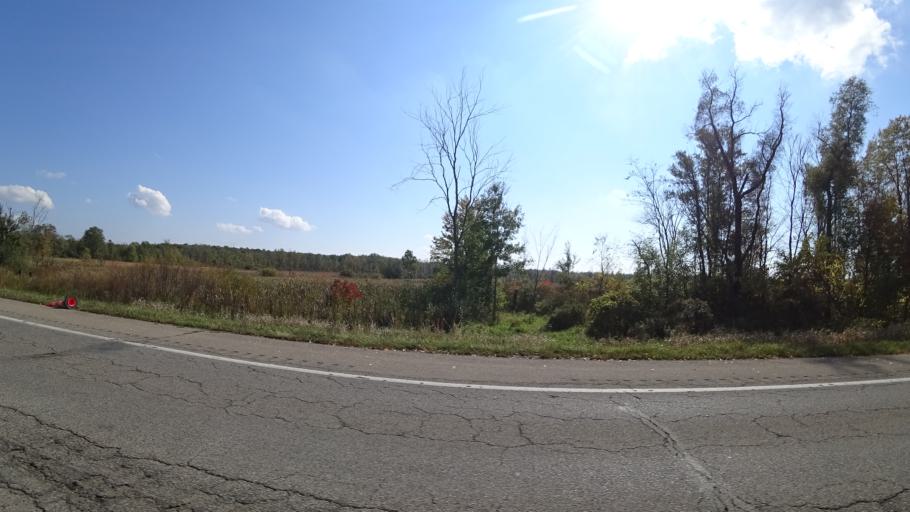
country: US
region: Michigan
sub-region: Calhoun County
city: Homer
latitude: 42.1461
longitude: -84.8359
